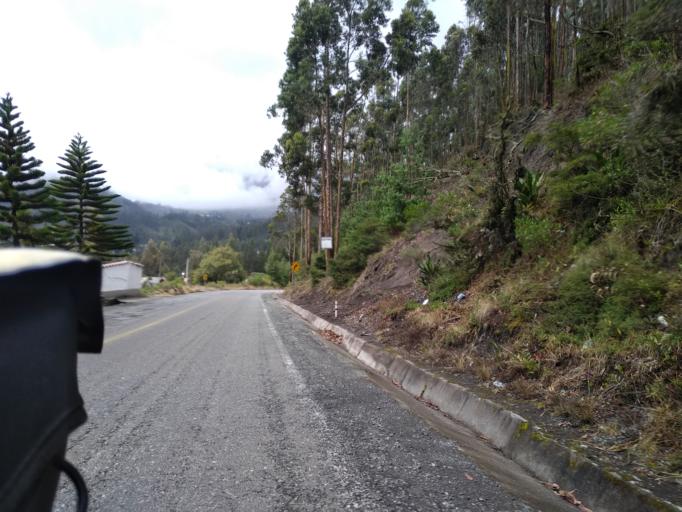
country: EC
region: Chimborazo
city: Guano
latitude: -1.5301
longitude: -78.5194
